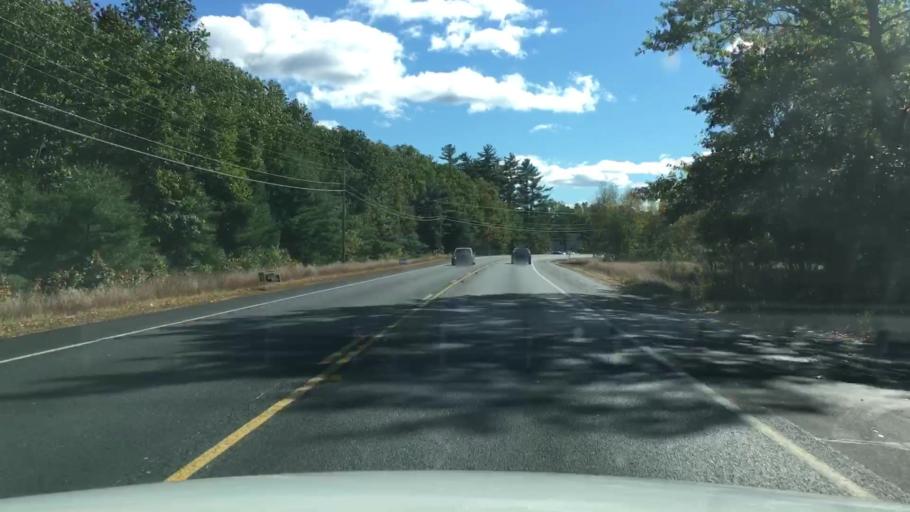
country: US
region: Maine
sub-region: York County
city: Alfred
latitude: 43.4628
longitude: -70.7196
